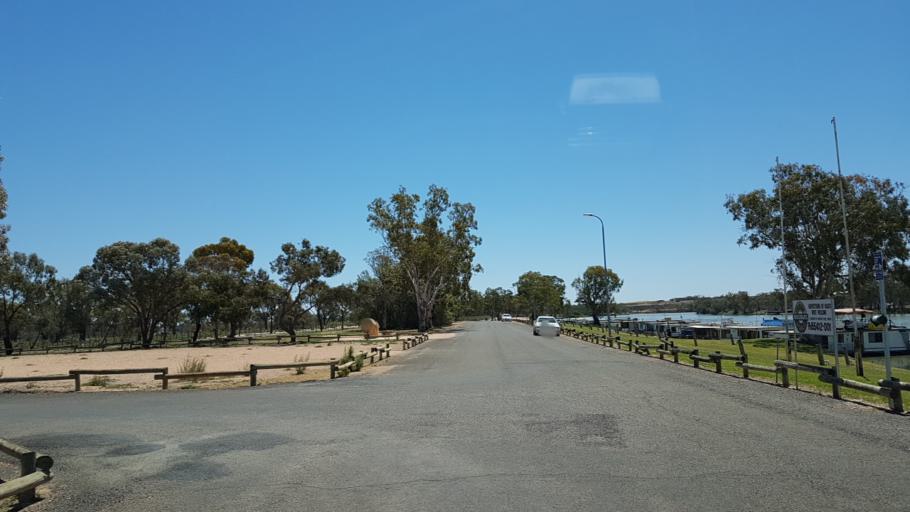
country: AU
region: South Australia
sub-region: Loxton Waikerie
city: Waikerie
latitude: -34.1720
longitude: 139.9808
